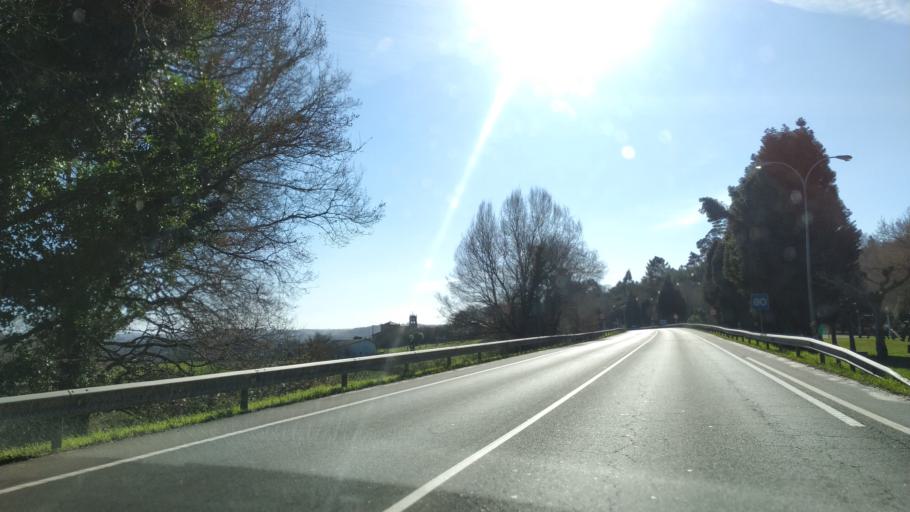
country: ES
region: Galicia
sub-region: Provincia de Pontevedra
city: Silleda
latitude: 42.6889
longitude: -8.2207
